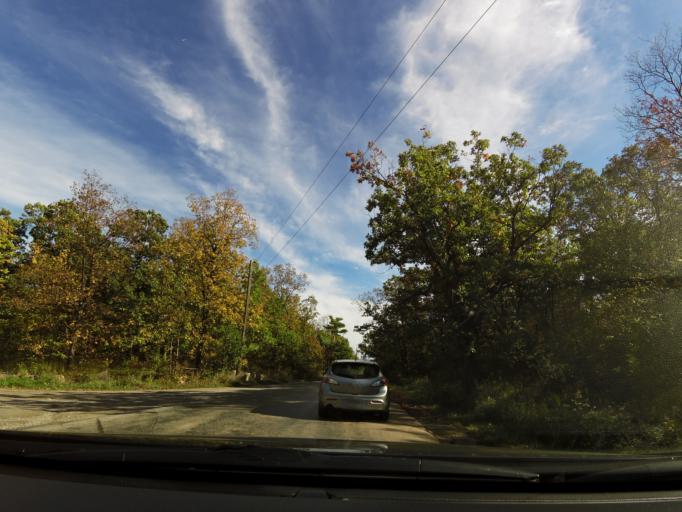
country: CA
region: Ontario
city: Burlington
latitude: 43.3329
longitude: -79.8483
